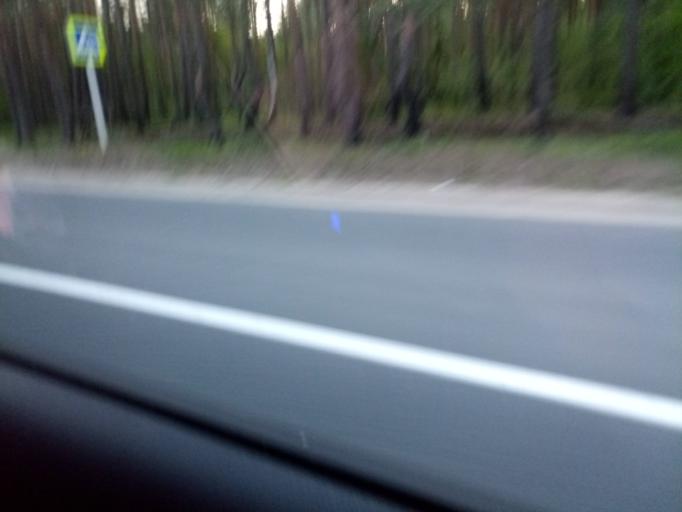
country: RU
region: Moskovskaya
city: Noginsk-9
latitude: 56.1006
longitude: 38.5846
